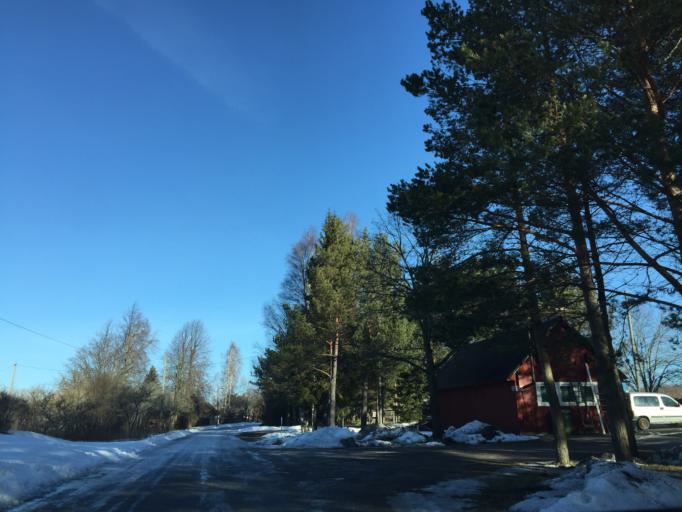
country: LV
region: Salacgrivas
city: Ainazi
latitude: 58.0825
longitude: 24.4892
